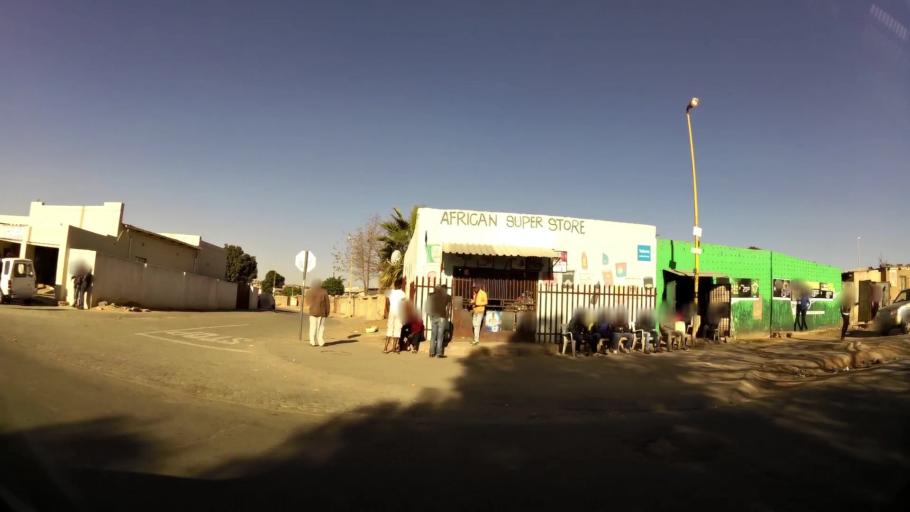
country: ZA
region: Gauteng
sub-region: Ekurhuleni Metropolitan Municipality
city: Tembisa
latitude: -26.0202
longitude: 28.2140
